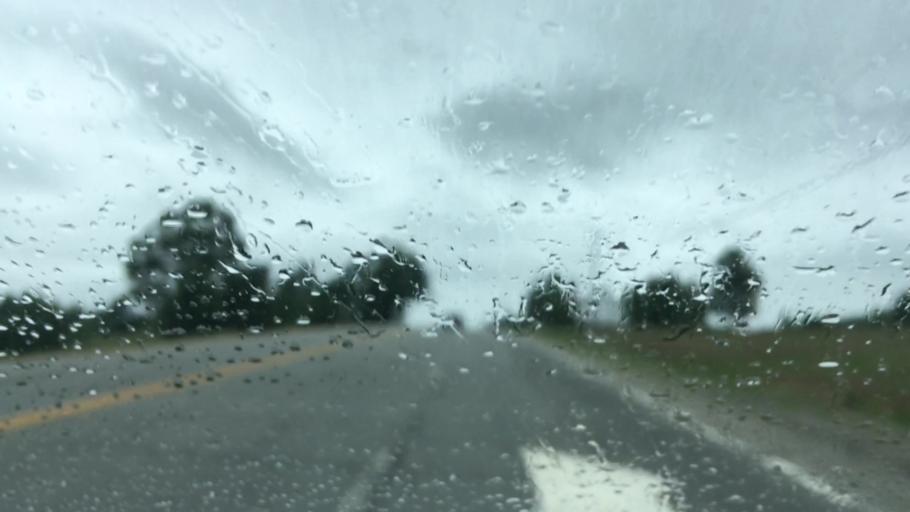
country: US
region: Maine
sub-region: Washington County
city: Cherryfield
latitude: 44.8466
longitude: -68.0632
